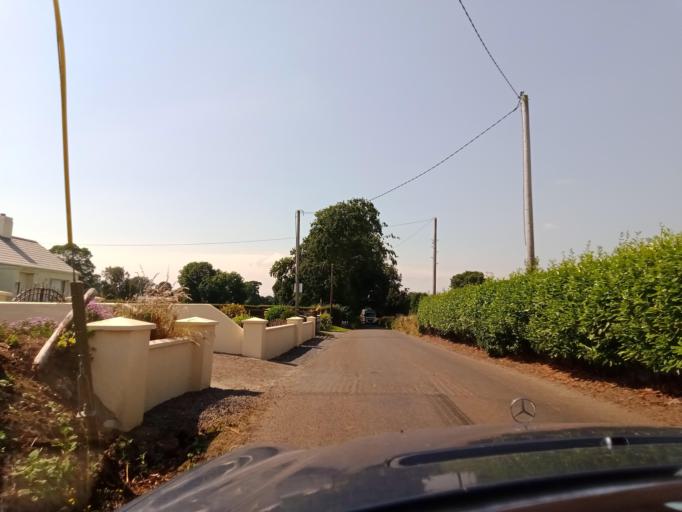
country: IE
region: Leinster
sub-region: Kilkenny
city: Piltown
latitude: 52.3399
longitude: -7.3130
